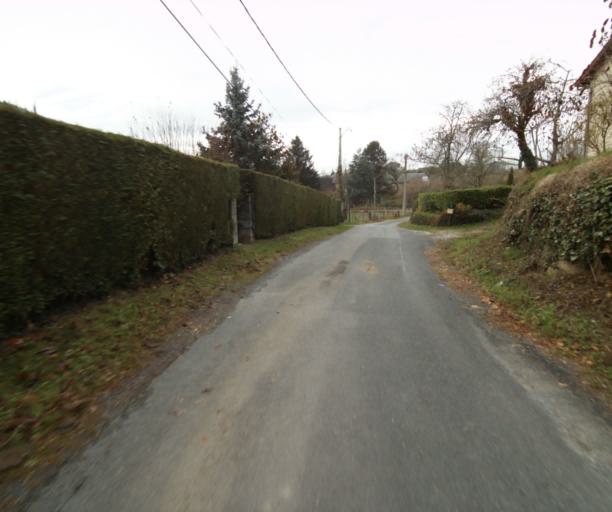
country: FR
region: Limousin
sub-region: Departement de la Correze
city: Chameyrat
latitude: 45.2351
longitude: 1.7000
